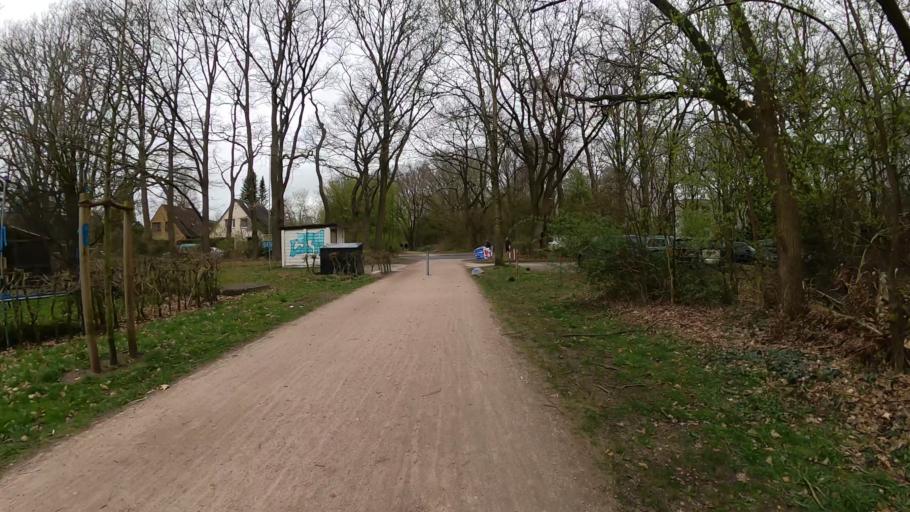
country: DE
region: Hamburg
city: Langenhorn
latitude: 53.6508
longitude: 10.0004
